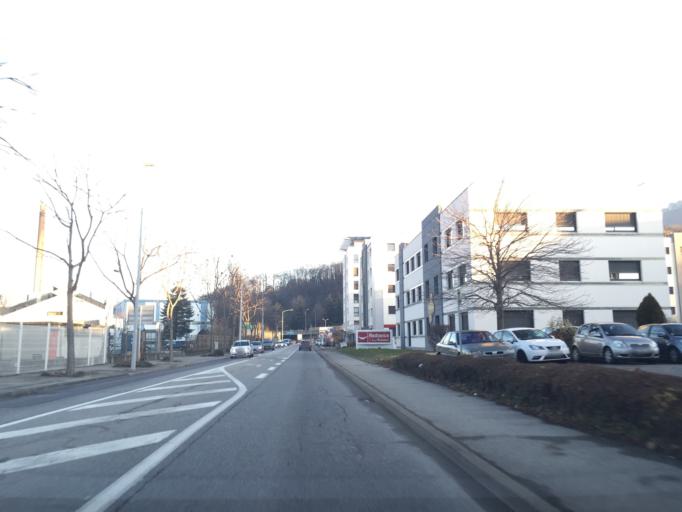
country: FR
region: Rhone-Alpes
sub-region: Departement de la Savoie
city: Cognin
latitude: 45.5814
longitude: 5.9089
